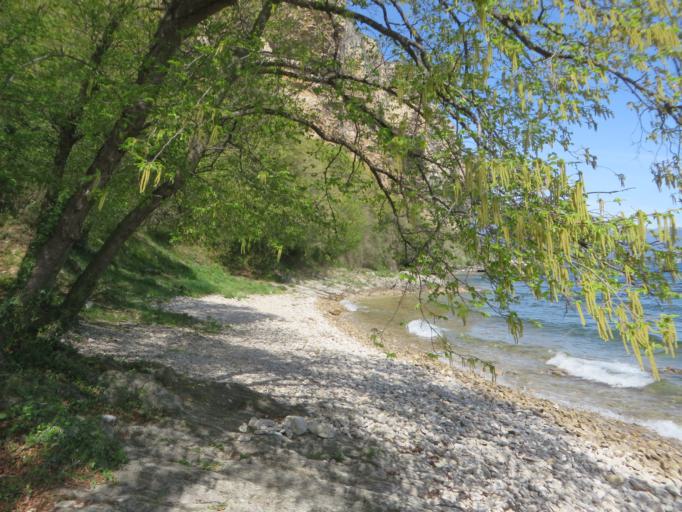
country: IT
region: Lombardy
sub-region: Provincia di Brescia
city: Solarolo
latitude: 45.5532
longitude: 10.5783
